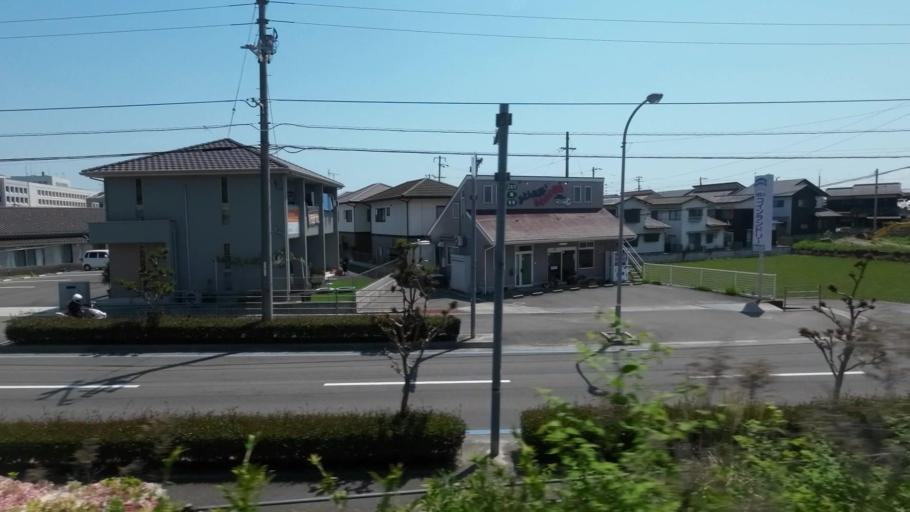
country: JP
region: Ehime
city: Hojo
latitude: 34.0839
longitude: 132.9843
